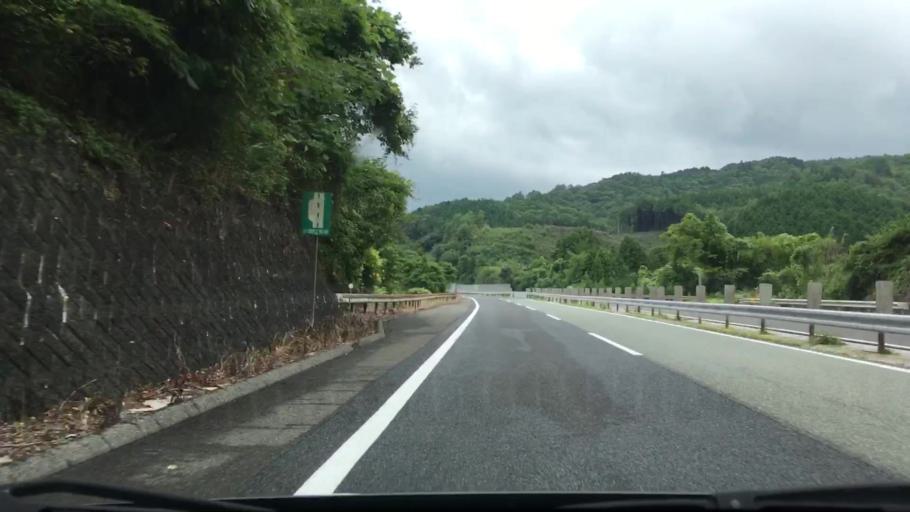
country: JP
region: Okayama
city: Niimi
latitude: 34.9426
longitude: 133.3287
